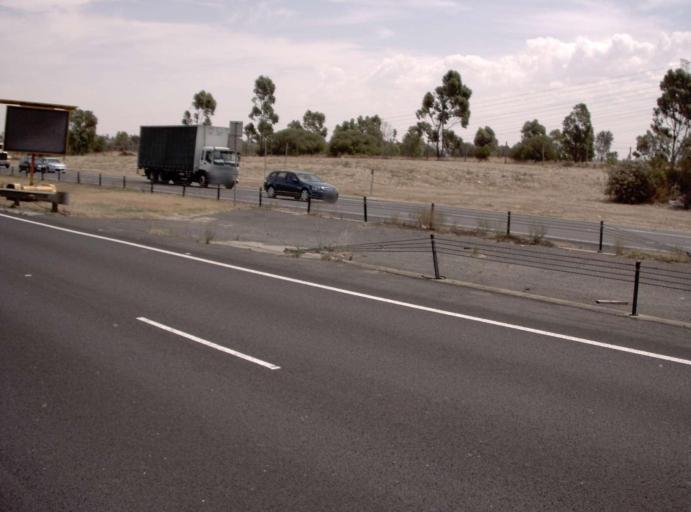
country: AU
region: Victoria
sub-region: Brimbank
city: Kealba
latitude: -37.7441
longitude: 144.8436
